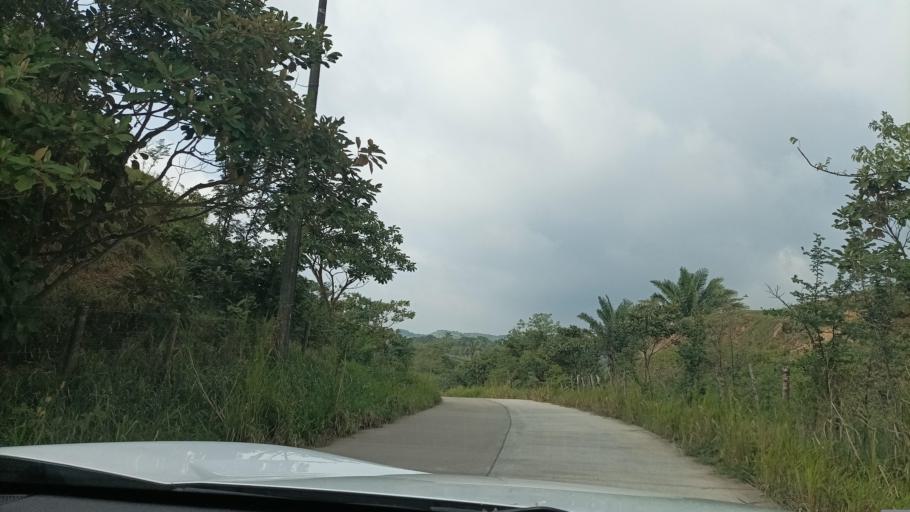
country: MX
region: Veracruz
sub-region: Moloacan
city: Tlacuilolapan
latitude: 18.0816
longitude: -94.2860
